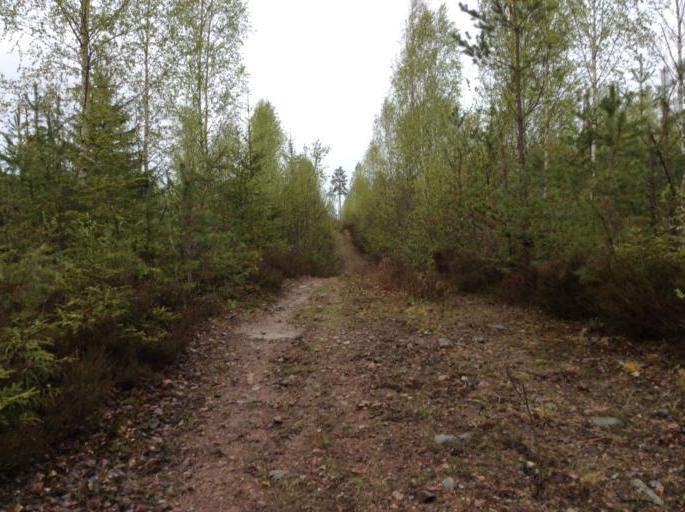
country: SE
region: Dalarna
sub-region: Avesta Kommun
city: Avesta
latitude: 60.1882
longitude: 16.1855
